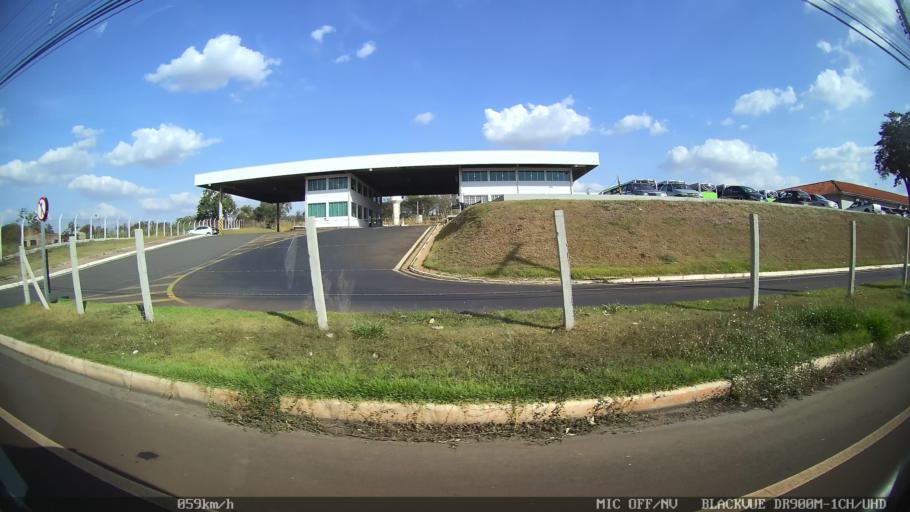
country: BR
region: Sao Paulo
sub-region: Ribeirao Preto
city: Ribeirao Preto
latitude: -21.1765
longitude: -47.8503
